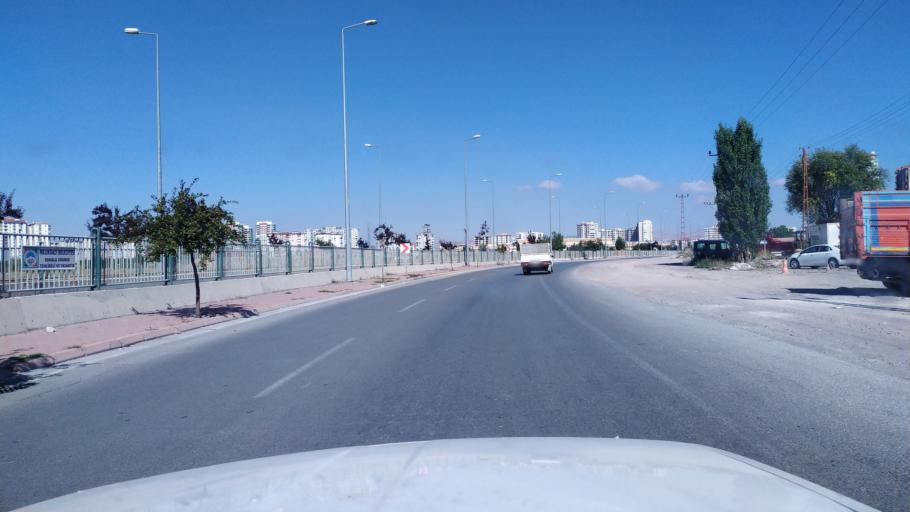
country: TR
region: Kayseri
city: Talas
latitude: 38.7349
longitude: 35.5466
